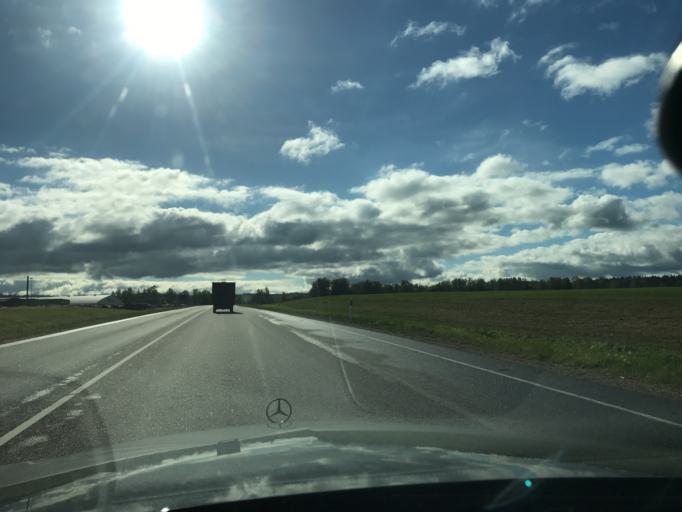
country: EE
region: Vorumaa
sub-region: Voru linn
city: Voru
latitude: 57.8178
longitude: 27.0645
